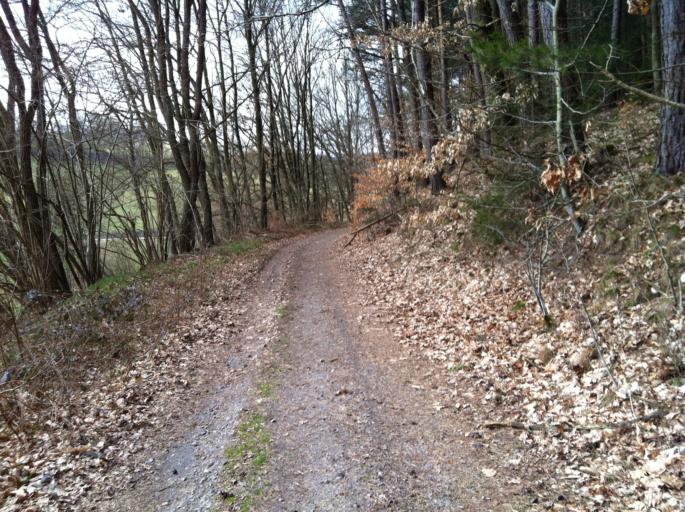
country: DE
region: Hesse
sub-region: Regierungsbezirk Darmstadt
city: Beerfelden
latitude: 49.6208
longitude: 8.9159
